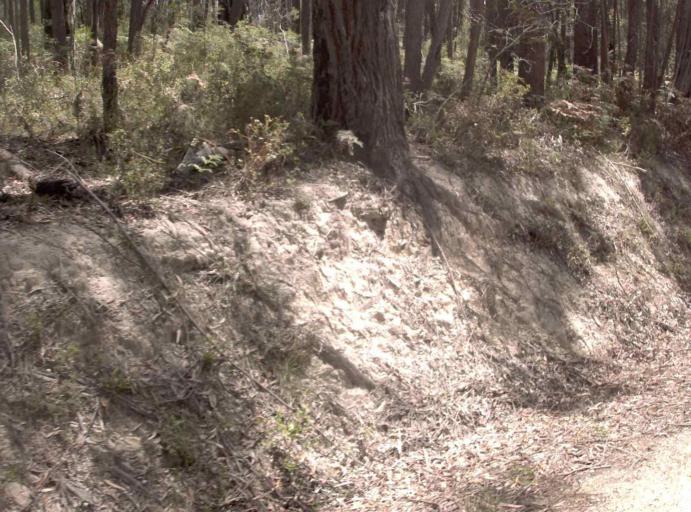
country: AU
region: New South Wales
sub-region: Bombala
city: Bombala
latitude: -37.5615
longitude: 148.9449
